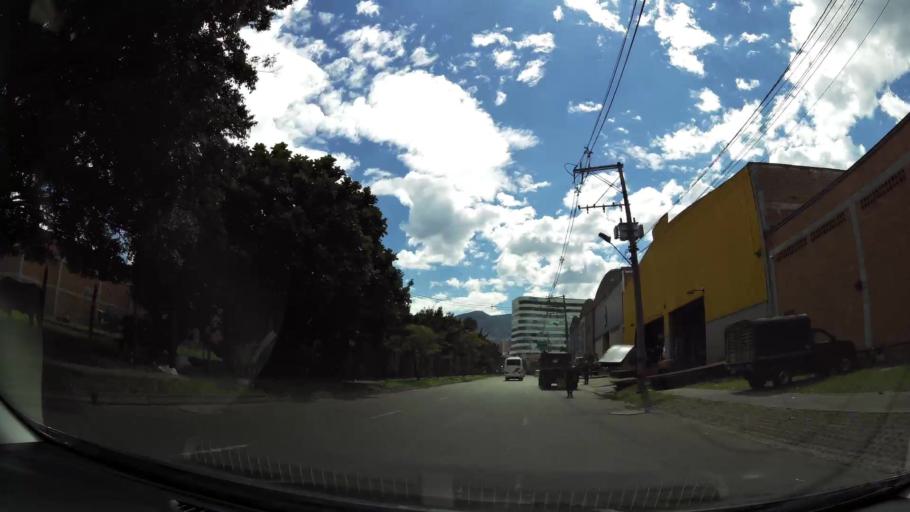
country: CO
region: Antioquia
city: Sabaneta
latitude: 6.1582
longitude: -75.6122
